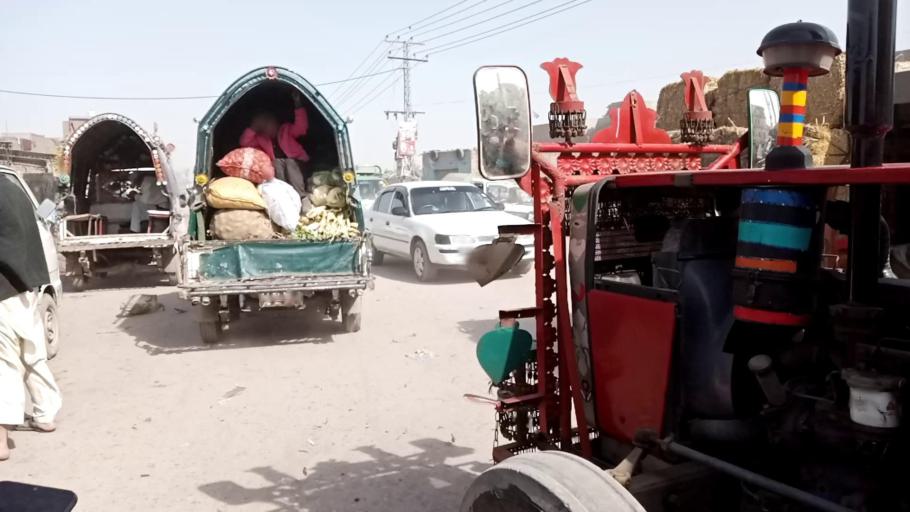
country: PK
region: Khyber Pakhtunkhwa
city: Peshawar
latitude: 33.9933
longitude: 71.6335
